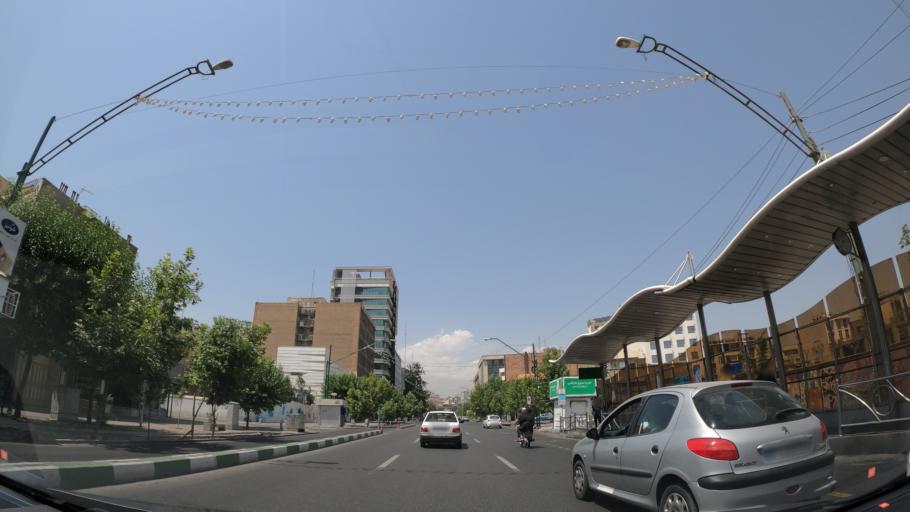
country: IR
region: Tehran
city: Tehran
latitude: 35.7245
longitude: 51.4140
